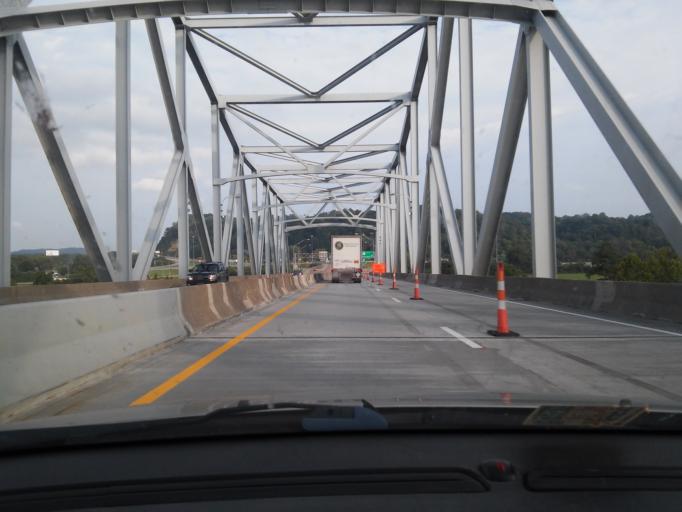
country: US
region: West Virginia
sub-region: Mason County
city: Point Pleasant
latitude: 38.8339
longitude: -82.1466
